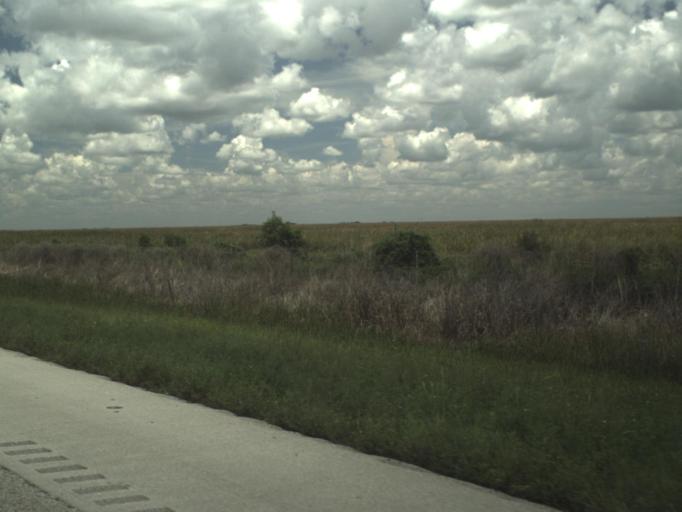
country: US
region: Florida
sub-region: Broward County
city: Weston
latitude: 26.1466
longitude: -80.6508
